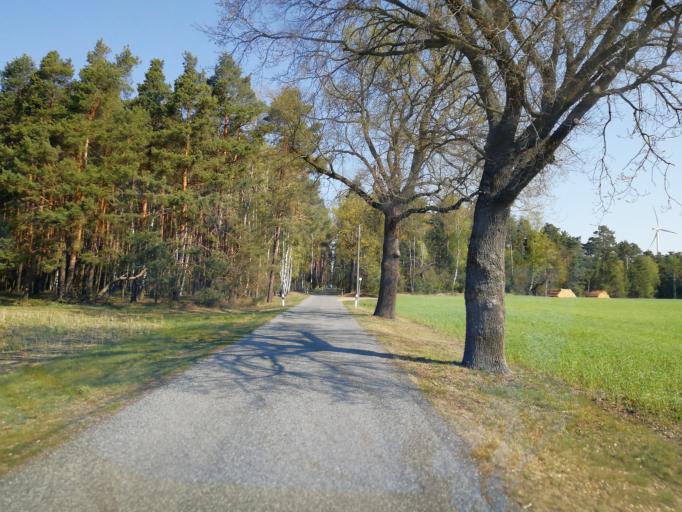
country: DE
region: Brandenburg
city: Bronkow
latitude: 51.6696
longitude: 13.8639
